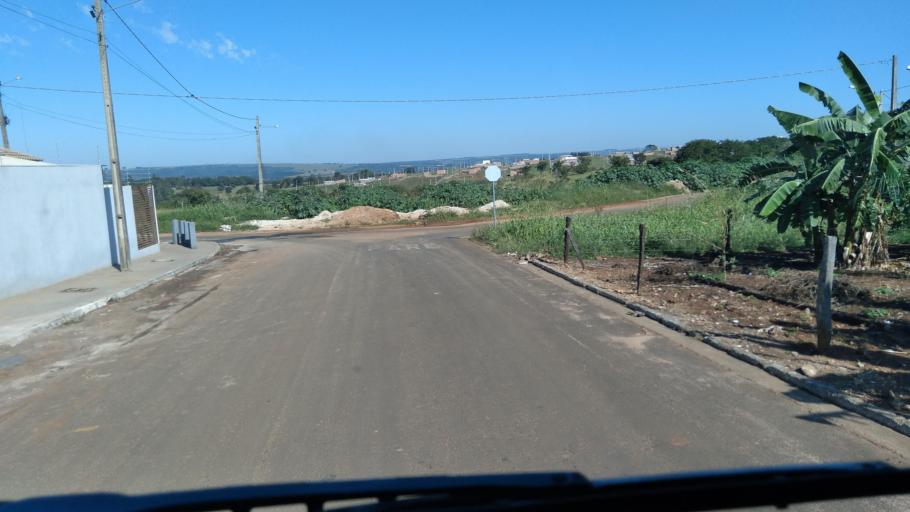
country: BR
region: Goias
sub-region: Mineiros
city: Mineiros
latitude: -17.5740
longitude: -52.5758
